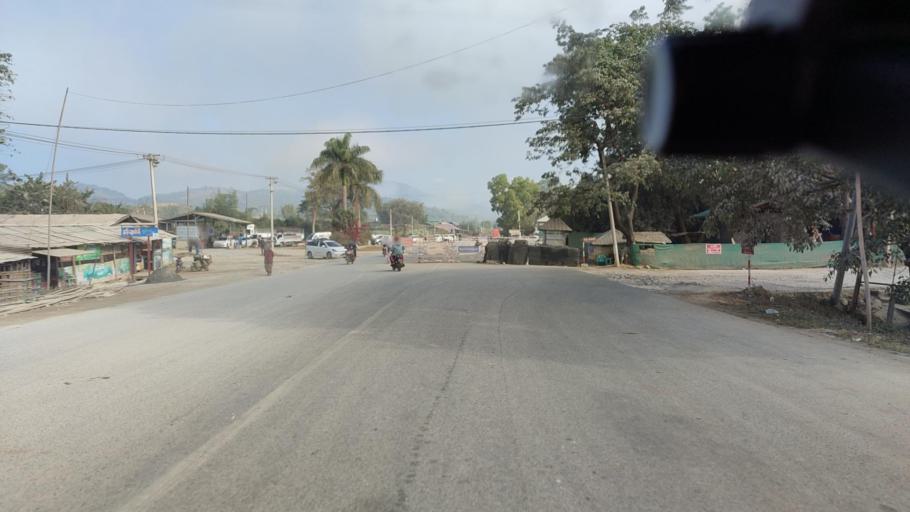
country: MM
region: Shan
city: Lashio
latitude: 23.2228
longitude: 97.9039
